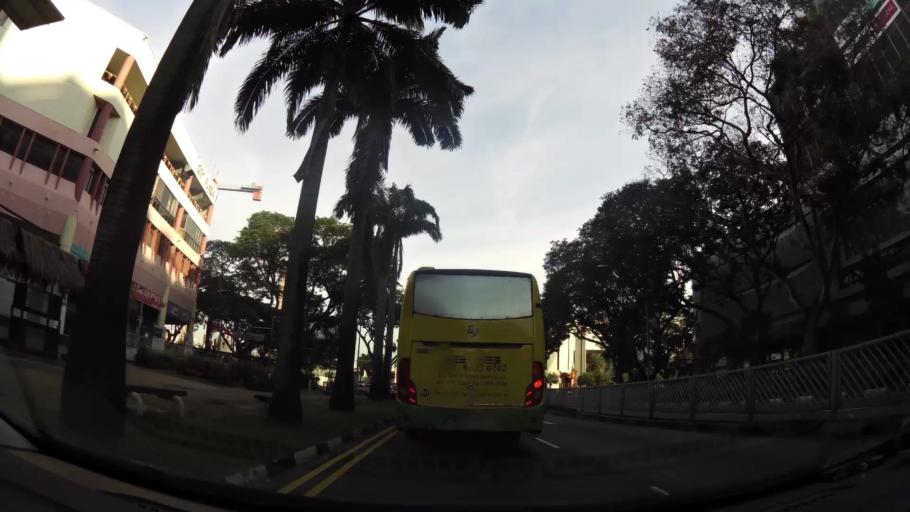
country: SG
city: Singapore
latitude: 1.3148
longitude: 103.8940
